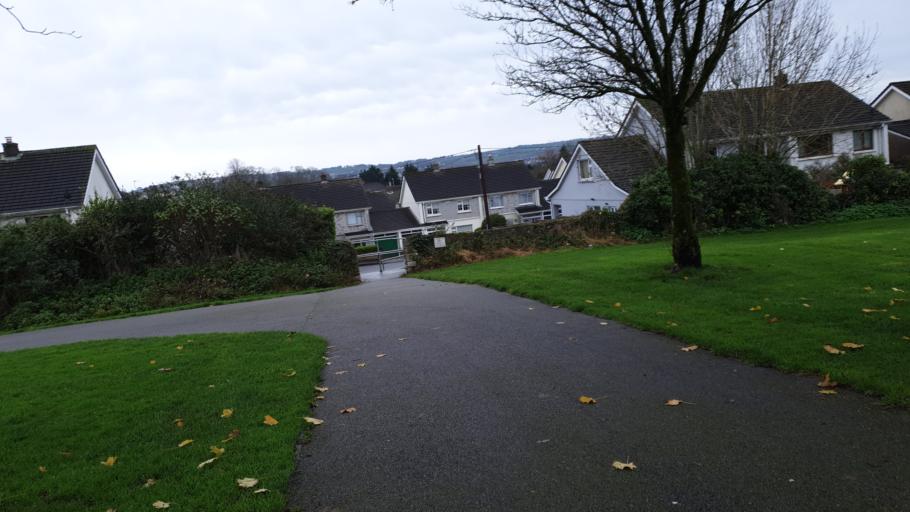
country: IE
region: Munster
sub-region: County Cork
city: Cork
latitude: 51.8886
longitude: -8.4307
